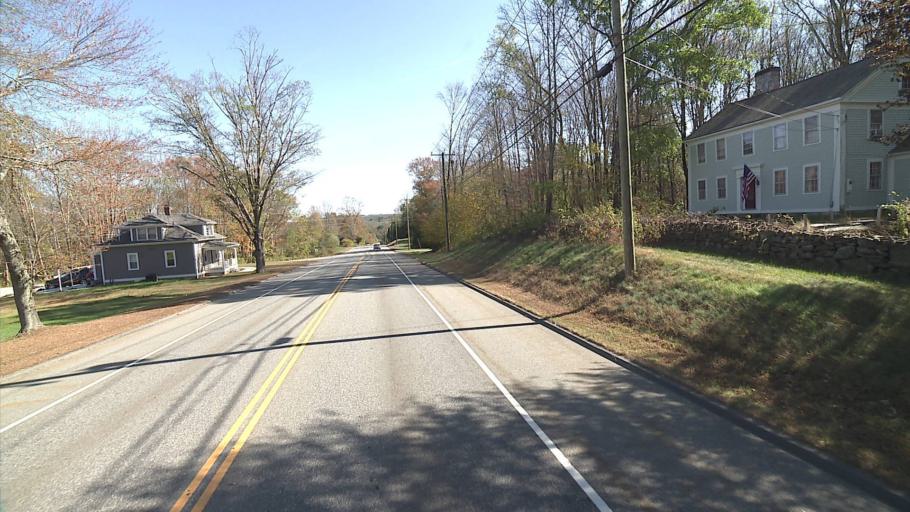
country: US
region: Connecticut
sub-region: Windham County
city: Wauregan
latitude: 41.7833
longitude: -71.9703
